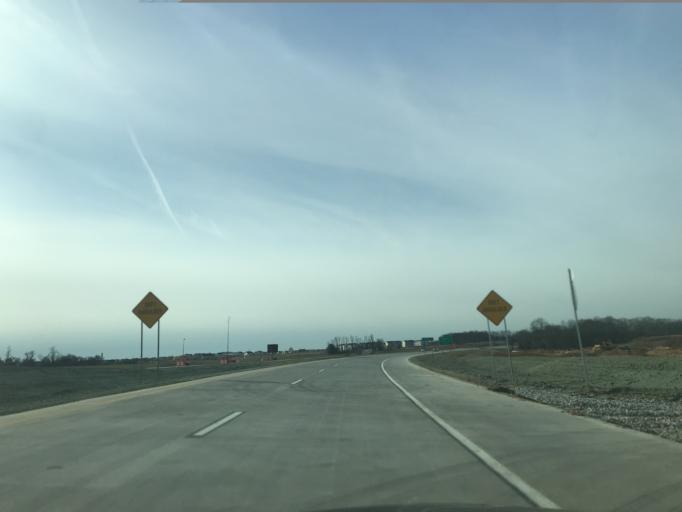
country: US
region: Delaware
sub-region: New Castle County
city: Delaware City
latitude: 39.5278
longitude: -75.6529
